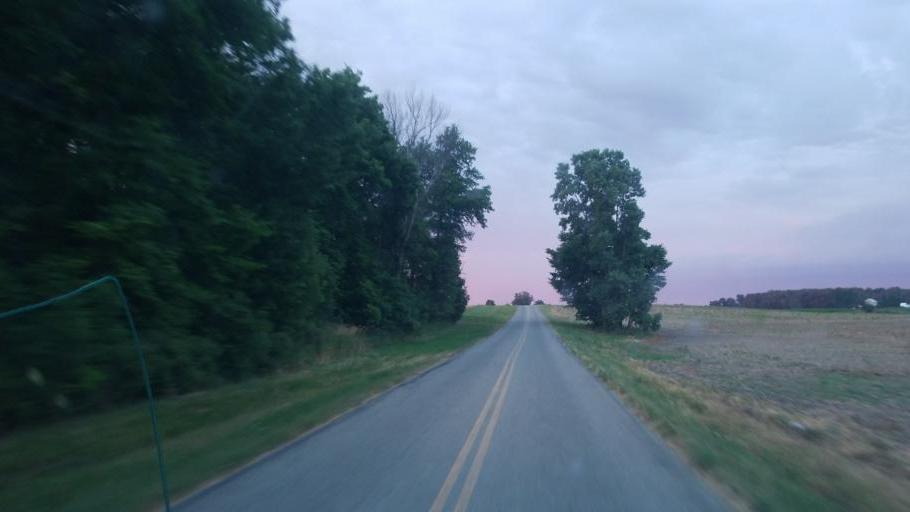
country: US
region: Ohio
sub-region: Defiance County
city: Hicksville
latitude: 41.3316
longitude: -84.8040
